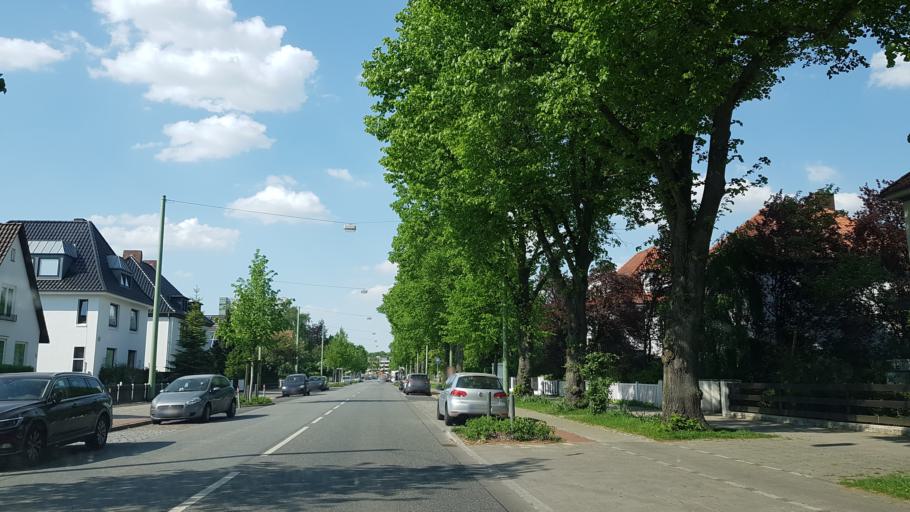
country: DE
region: Lower Saxony
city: Langen
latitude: 53.5771
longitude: 8.5920
